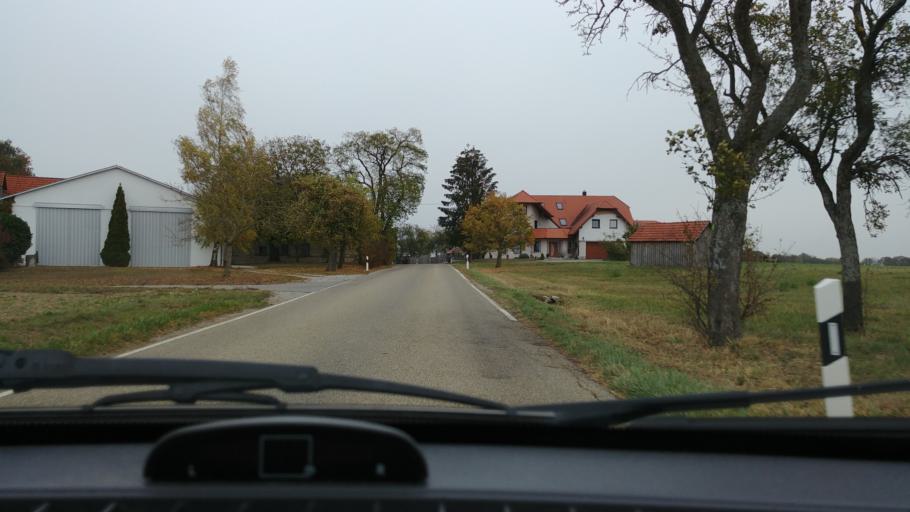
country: DE
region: Baden-Wuerttemberg
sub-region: Regierungsbezirk Stuttgart
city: Rot am See
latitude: 49.2974
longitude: 10.0829
